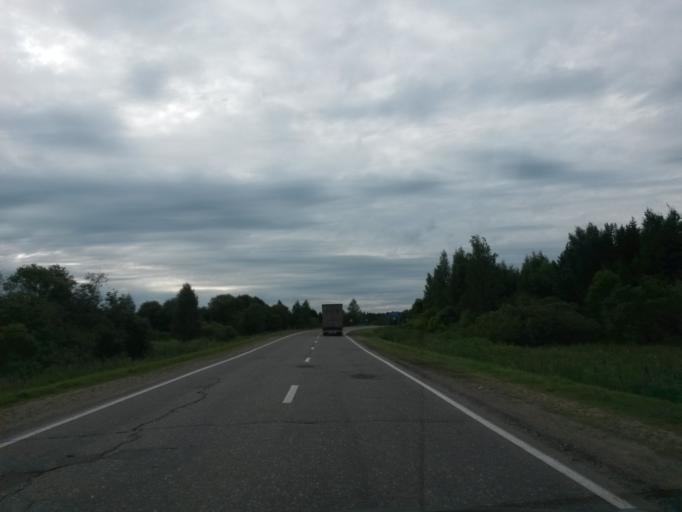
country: RU
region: Jaroslavl
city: Krasnyye Tkachi
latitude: 57.3721
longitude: 39.7298
